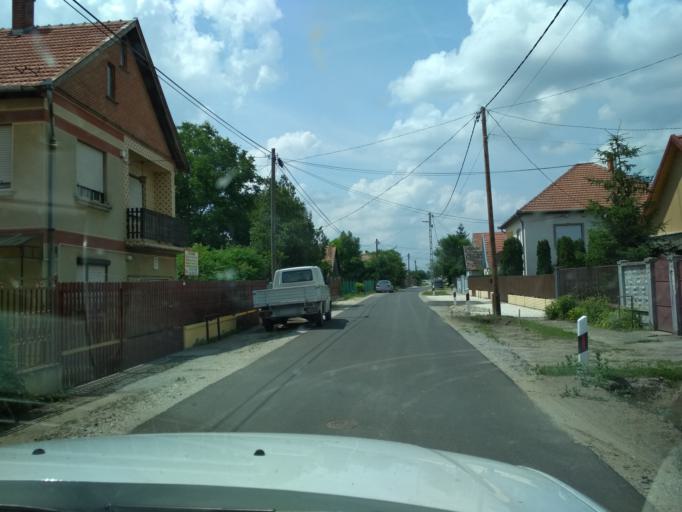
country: HU
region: Pest
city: Tapioszentmarton
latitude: 47.3452
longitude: 19.7423
